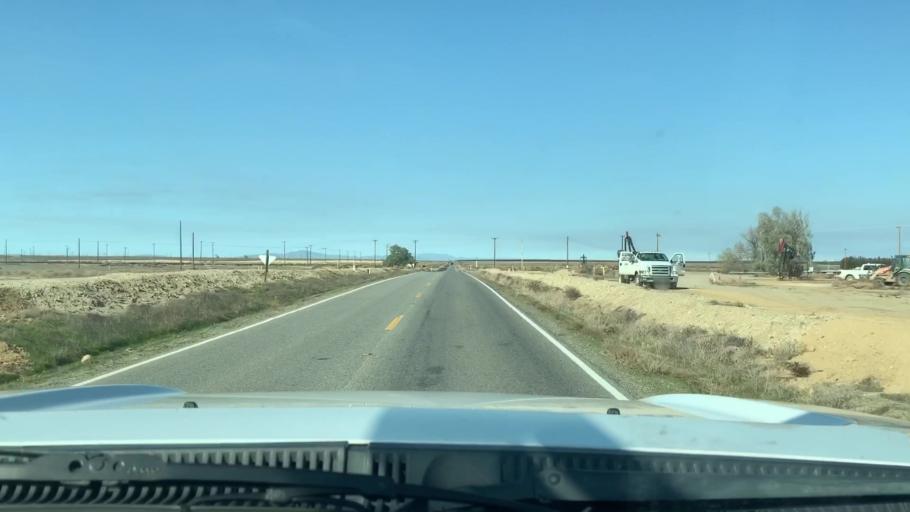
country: US
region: California
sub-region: Kern County
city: Lost Hills
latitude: 35.5407
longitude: -119.7764
